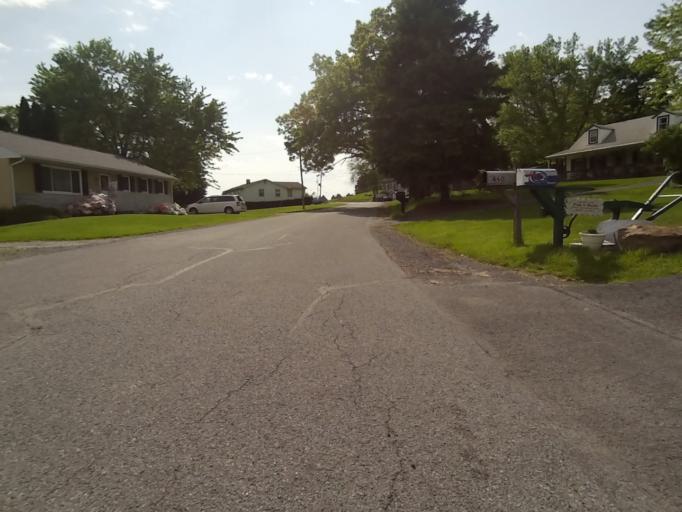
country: US
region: Pennsylvania
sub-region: Centre County
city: Lemont
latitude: 40.8357
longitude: -77.7941
